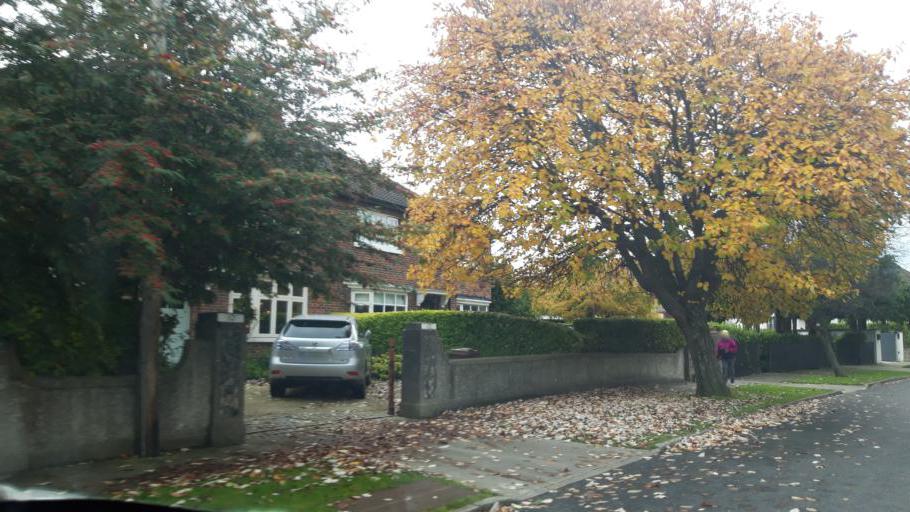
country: IE
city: Milltown
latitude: 53.3107
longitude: -6.2398
